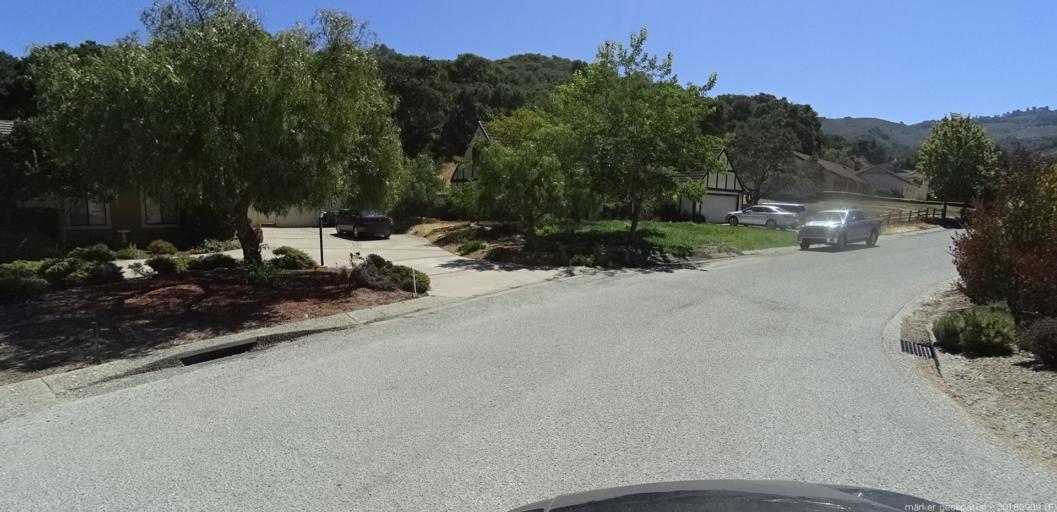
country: US
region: California
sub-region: Monterey County
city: Carmel Valley Village
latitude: 36.5645
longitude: -121.7546
